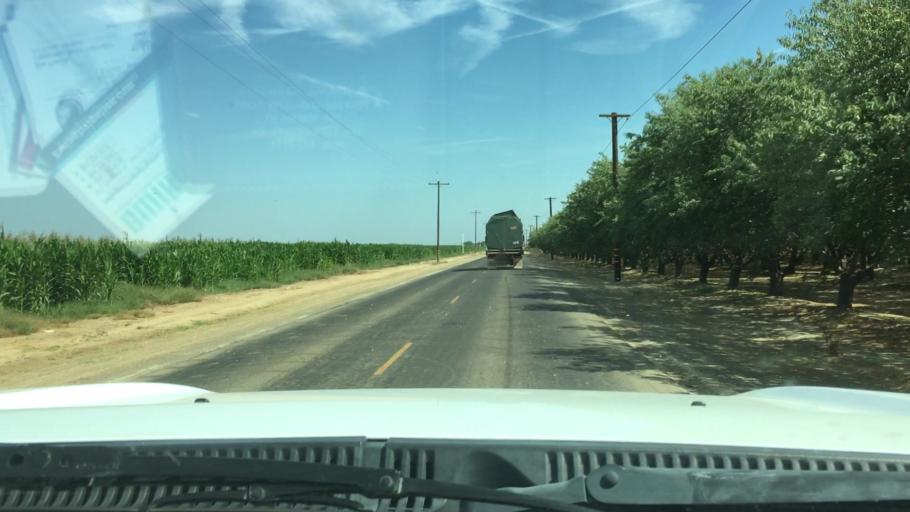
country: US
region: California
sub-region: Kern County
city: Shafter
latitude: 35.4797
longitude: -119.3680
